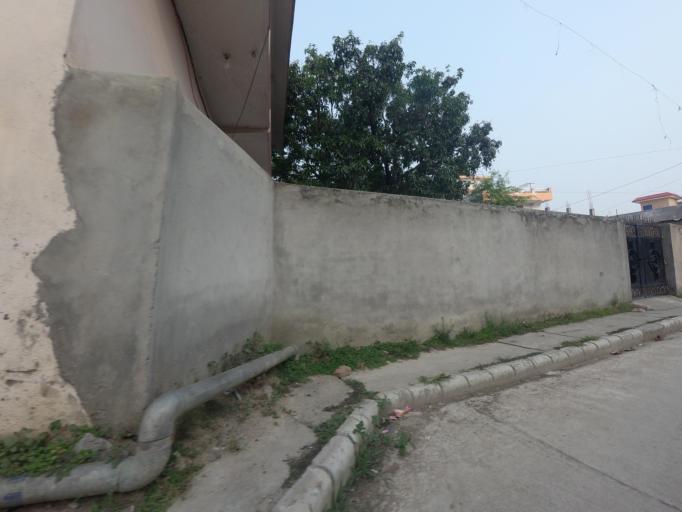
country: NP
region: Western Region
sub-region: Lumbini Zone
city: Bhairahawa
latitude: 27.5166
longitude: 83.4460
